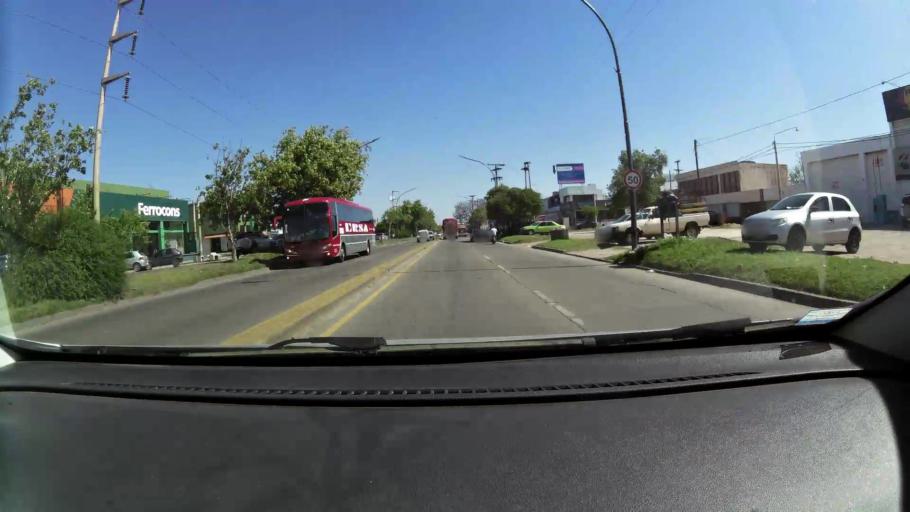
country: AR
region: Cordoba
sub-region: Departamento de Capital
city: Cordoba
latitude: -31.3776
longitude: -64.1761
